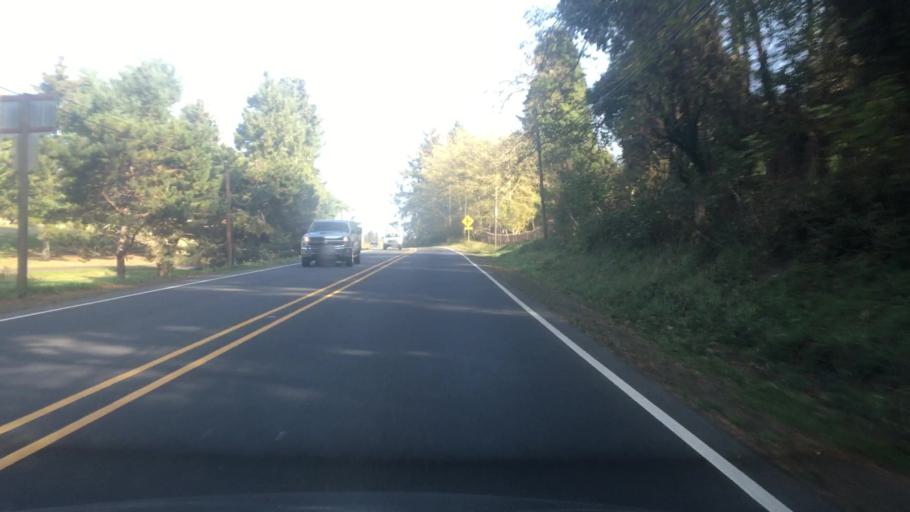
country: US
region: Oregon
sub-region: Lincoln County
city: Lincoln City
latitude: 45.0002
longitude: -123.9894
